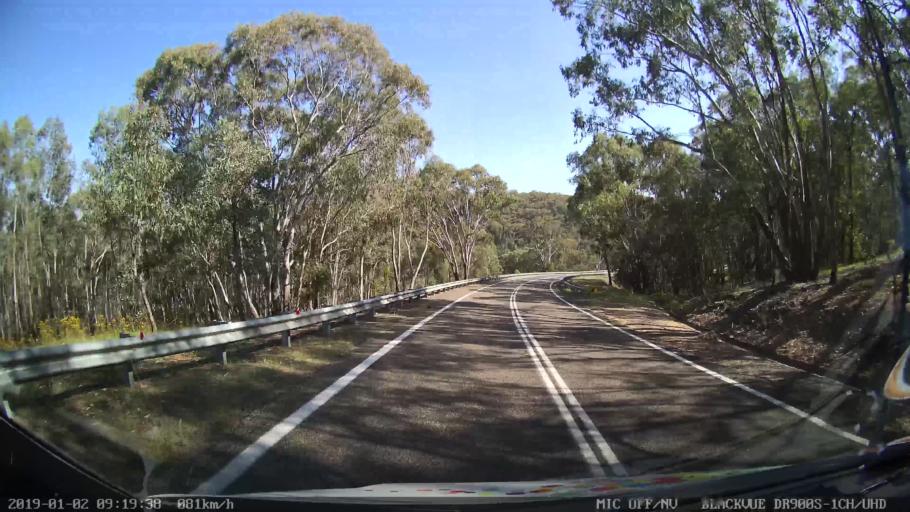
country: AU
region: New South Wales
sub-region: Tumut Shire
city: Tumut
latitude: -35.4202
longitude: 148.2766
